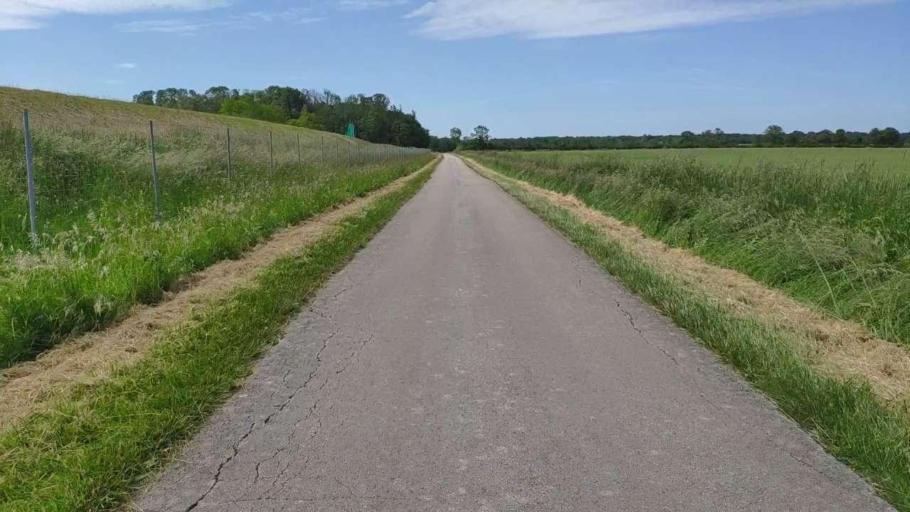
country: FR
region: Franche-Comte
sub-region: Departement du Jura
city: Bletterans
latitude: 46.6863
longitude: 5.4285
